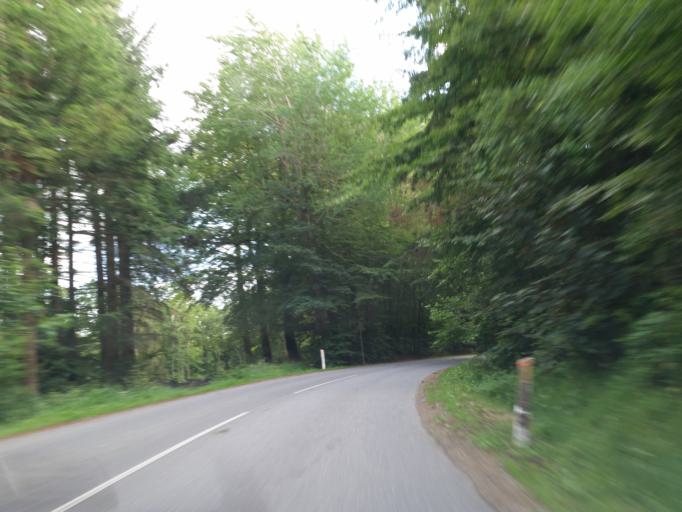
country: DK
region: South Denmark
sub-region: Vejle Kommune
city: Borkop
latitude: 55.6868
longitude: 9.6182
